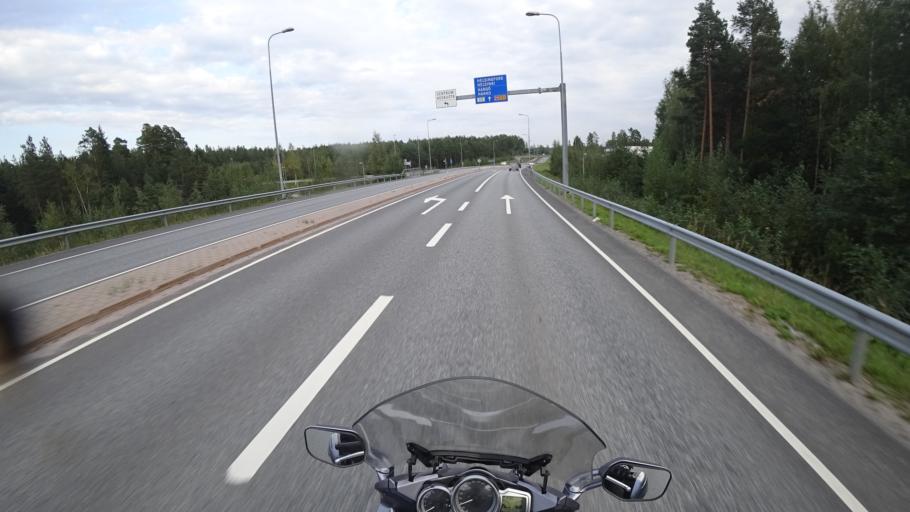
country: FI
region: Uusimaa
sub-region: Raaseporin
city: Karis
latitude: 60.0612
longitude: 23.6361
